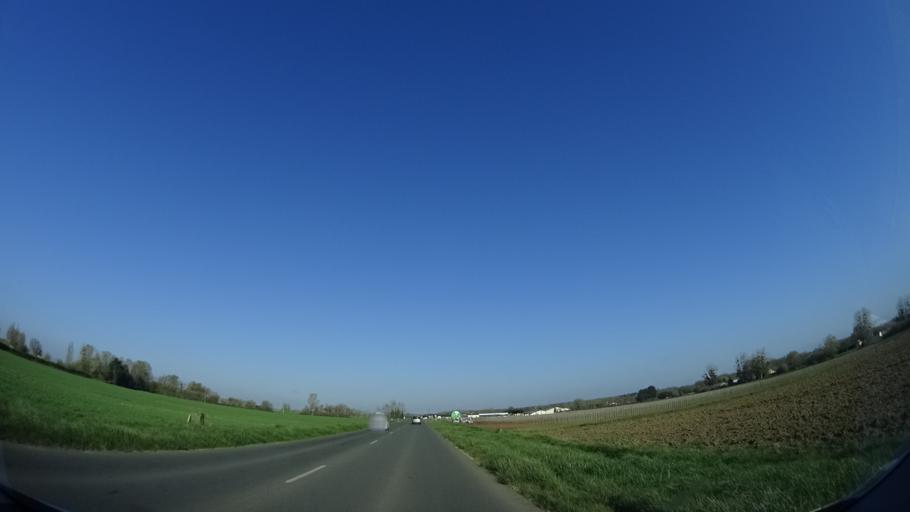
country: FR
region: Pays de la Loire
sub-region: Departement de Maine-et-Loire
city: Doue-la-Fontaine
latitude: 47.2054
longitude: -0.2910
